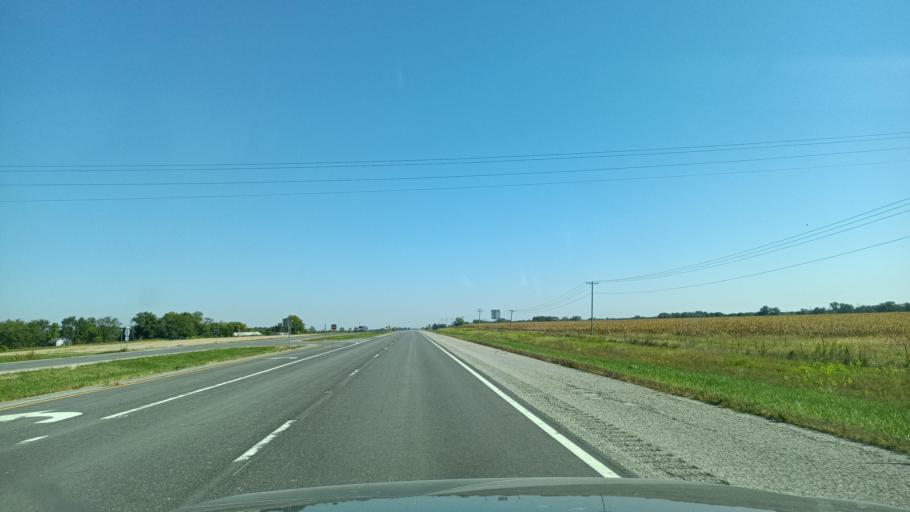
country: US
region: Illinois
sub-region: Adams County
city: Camp Point
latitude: 40.1698
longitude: -91.2032
